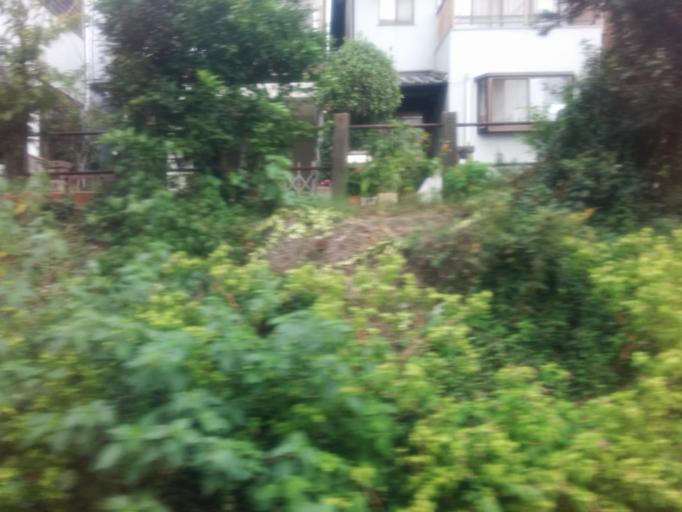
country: JP
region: Kyoto
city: Uji
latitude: 34.9336
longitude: 135.7696
